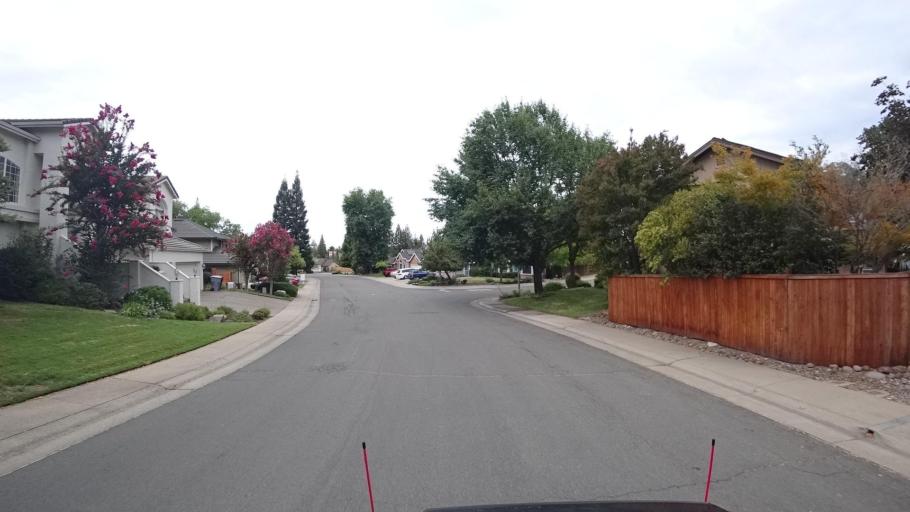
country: US
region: California
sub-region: Placer County
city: Rocklin
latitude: 38.7919
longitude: -121.2571
